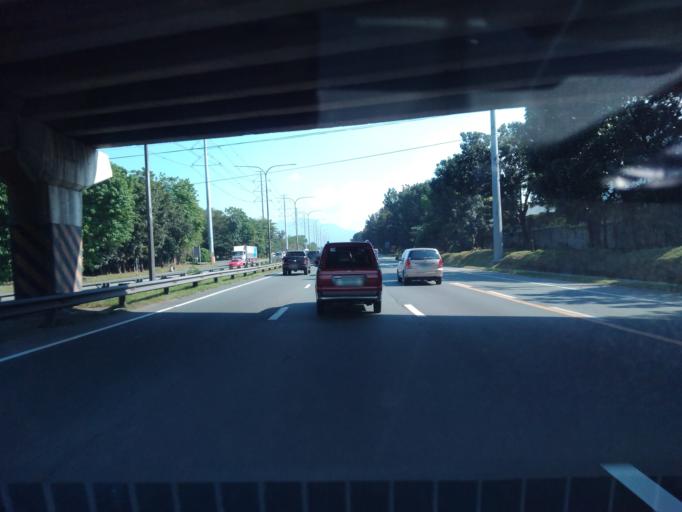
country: PH
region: Calabarzon
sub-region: Province of Laguna
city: Cabuyao
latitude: 14.2417
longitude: 121.1111
